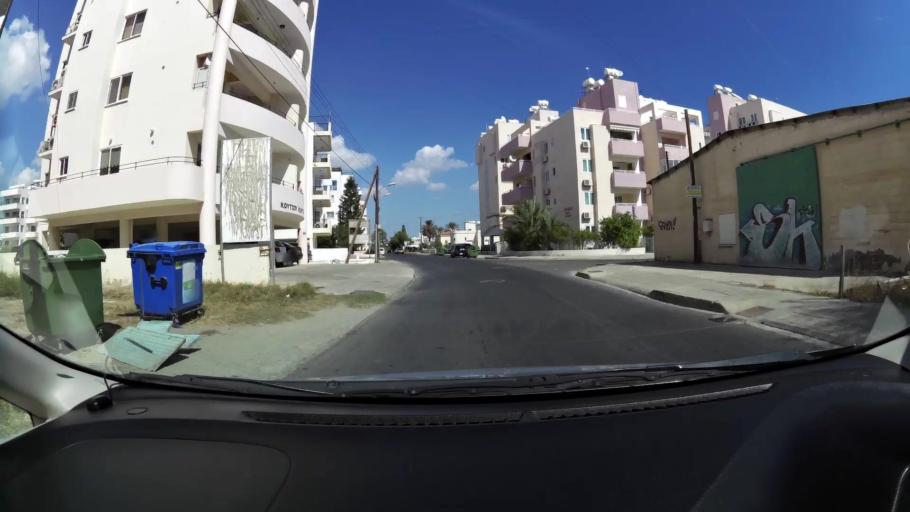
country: CY
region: Larnaka
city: Larnaca
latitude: 34.9031
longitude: 33.6349
